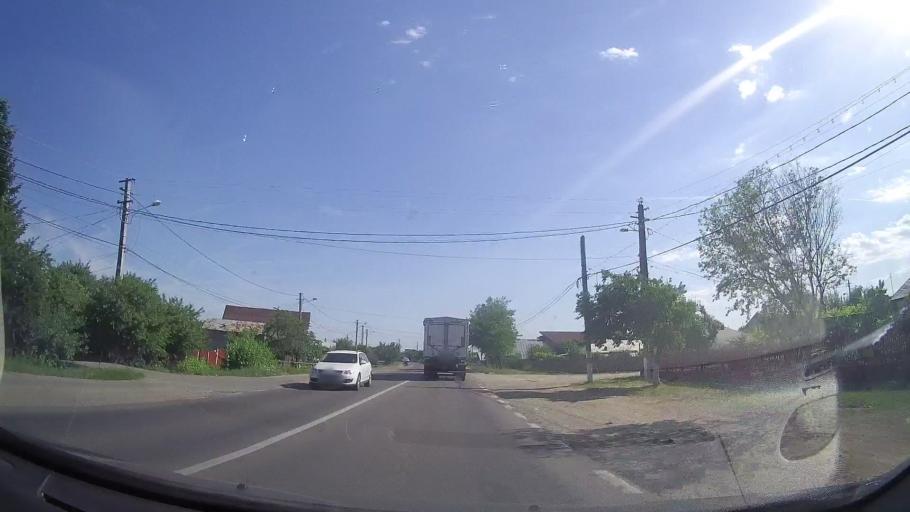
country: RO
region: Prahova
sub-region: Comuna Lipanesti
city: Sipotu
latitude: 45.0378
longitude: 26.0169
